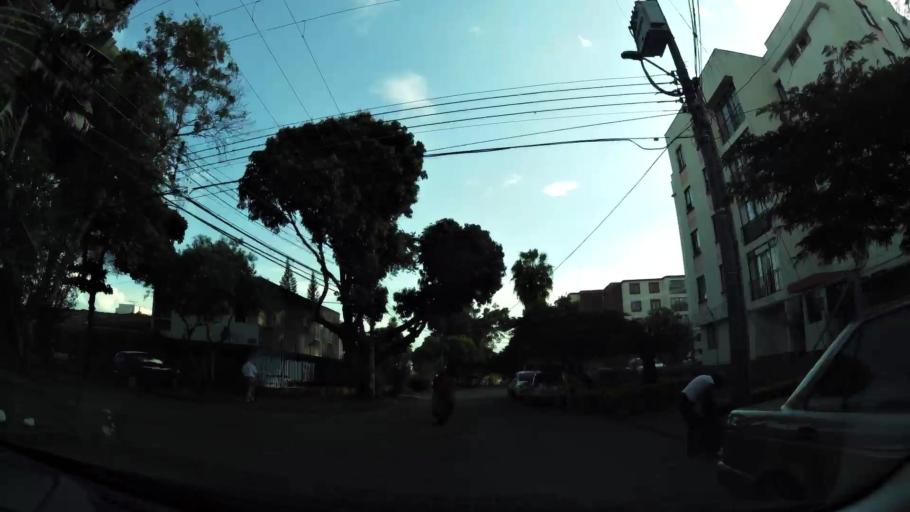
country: CO
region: Valle del Cauca
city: Cali
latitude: 3.4201
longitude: -76.5506
